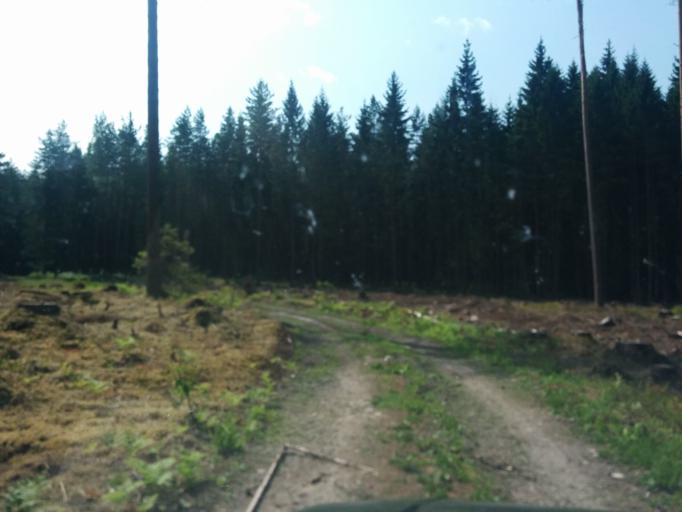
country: LV
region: Ikskile
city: Ikskile
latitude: 56.7435
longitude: 24.5005
